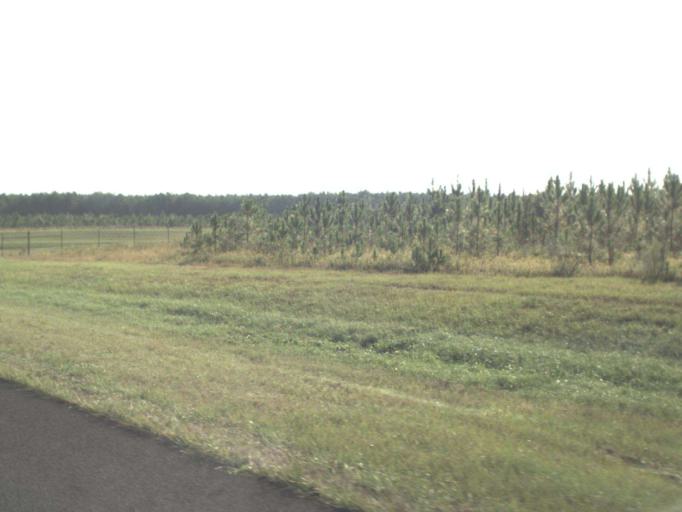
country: US
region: Florida
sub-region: Bay County
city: Laguna Beach
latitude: 30.4612
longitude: -85.8664
